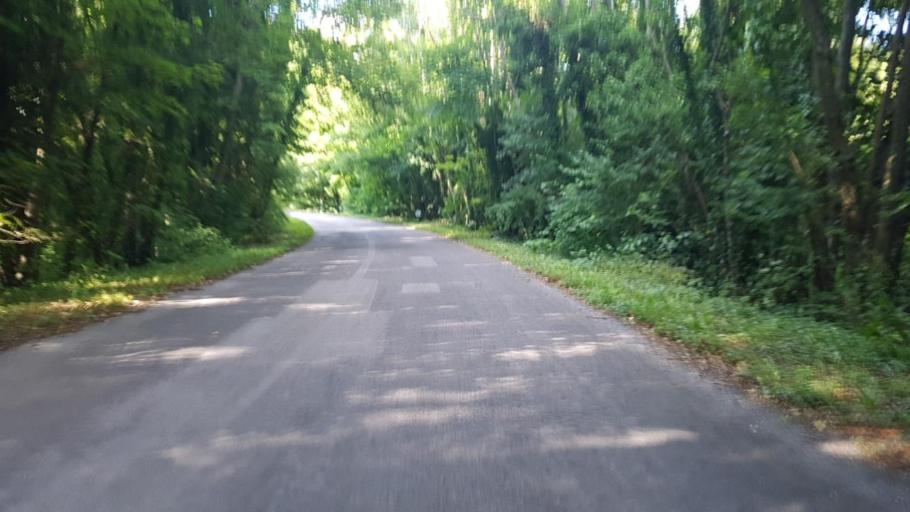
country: FR
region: Picardie
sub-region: Departement de l'Oise
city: Senlis
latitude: 49.1933
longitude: 2.6062
